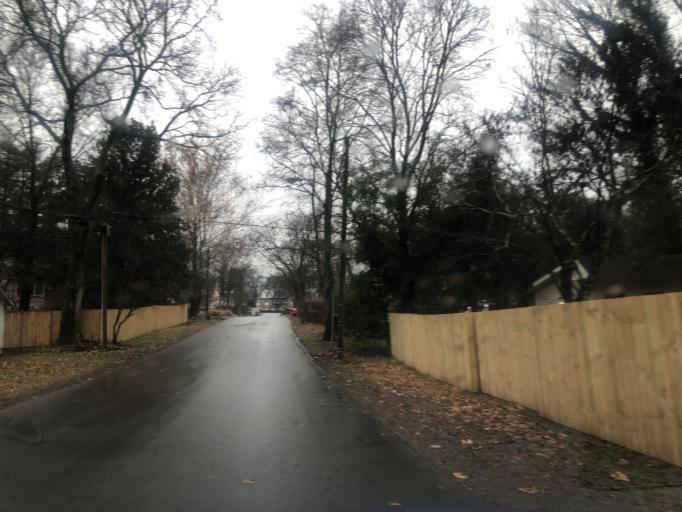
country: US
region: Tennessee
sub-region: Davidson County
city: Nashville
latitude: 36.1278
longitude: -86.8089
